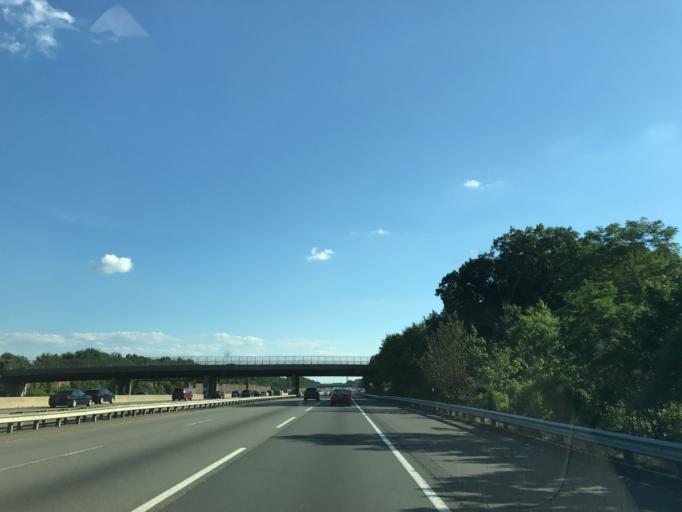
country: US
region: New Jersey
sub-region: Middlesex County
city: East Brunswick
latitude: 40.4331
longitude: -74.4344
